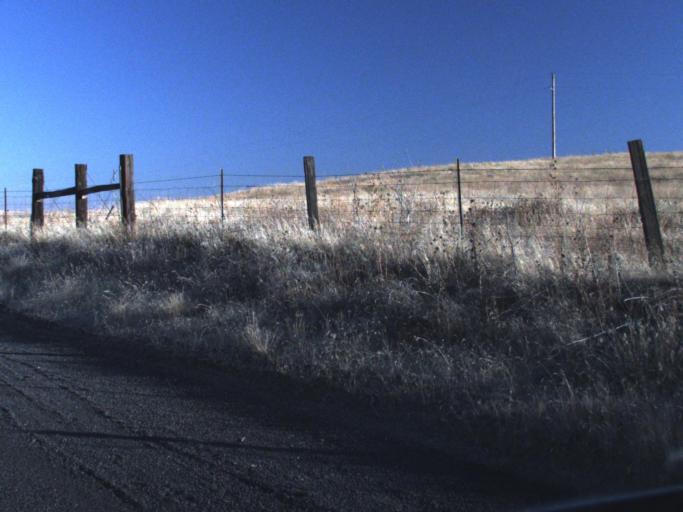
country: US
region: Washington
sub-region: Walla Walla County
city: Waitsburg
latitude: 46.6691
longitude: -118.2925
